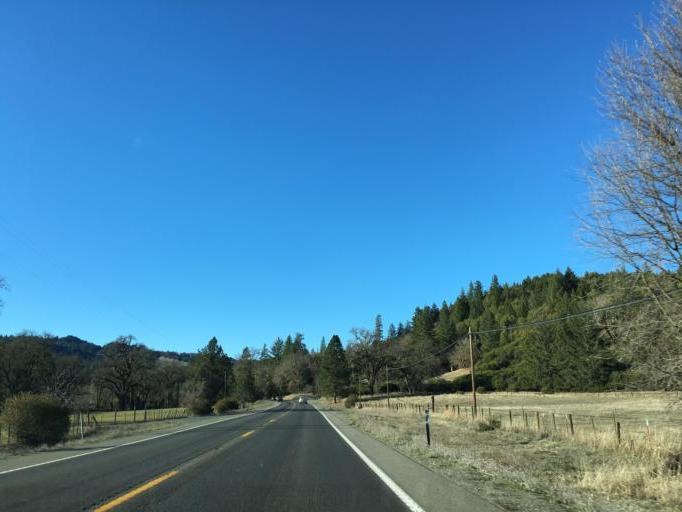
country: US
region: California
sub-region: Mendocino County
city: Laytonville
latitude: 39.7463
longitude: -123.5247
